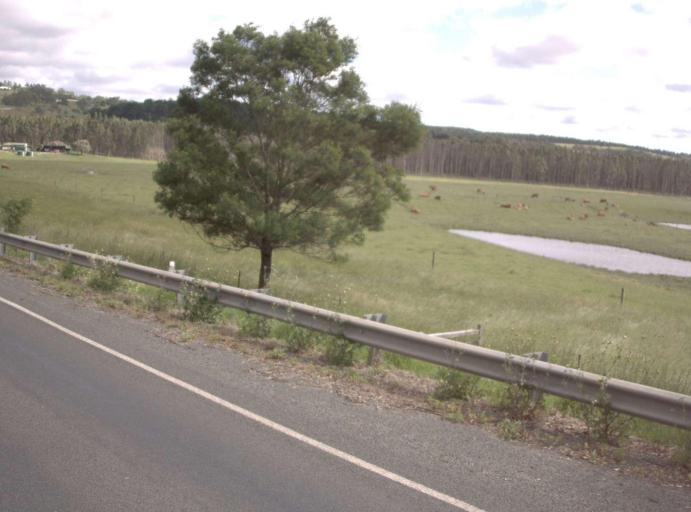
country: AU
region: Victoria
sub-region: Latrobe
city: Morwell
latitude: -38.1665
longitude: 146.4104
